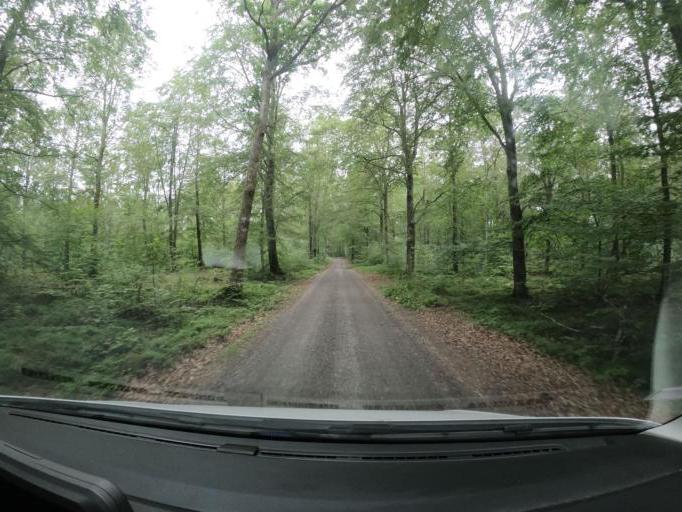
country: SE
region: Skane
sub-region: Perstorps Kommun
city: Perstorp
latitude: 56.1035
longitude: 13.5305
